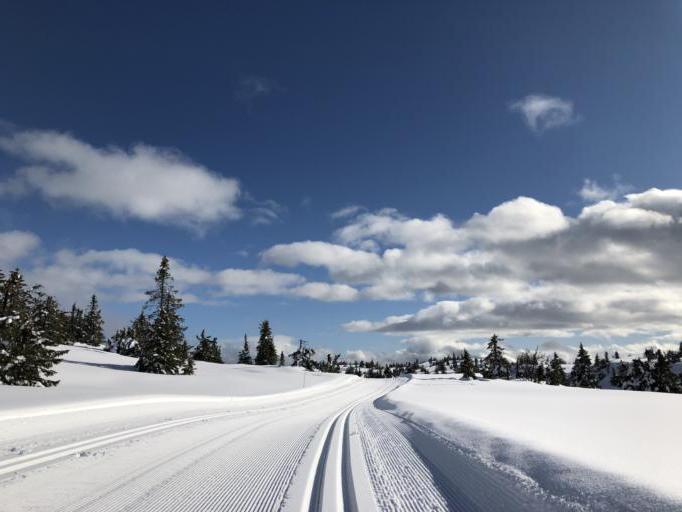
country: NO
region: Oppland
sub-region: Gausdal
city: Segalstad bru
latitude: 61.3317
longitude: 10.0313
